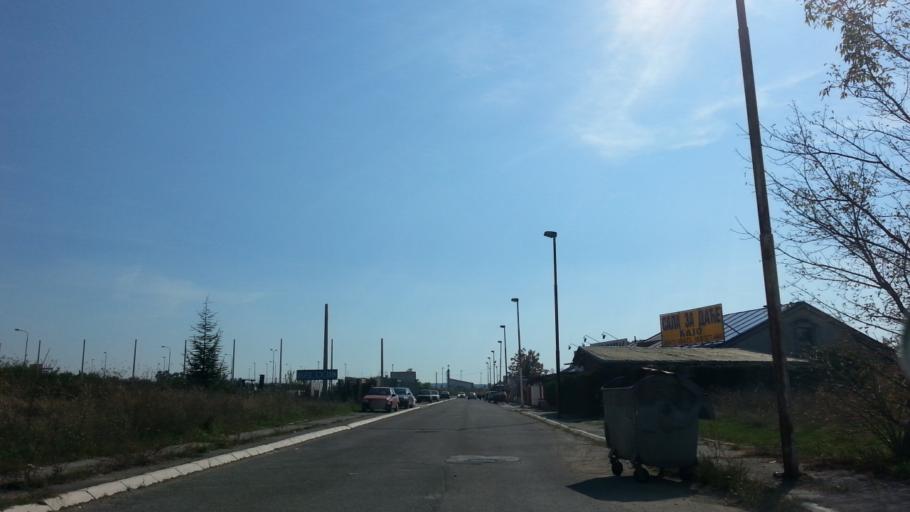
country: RS
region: Central Serbia
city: Sremcica
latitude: 44.7087
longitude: 20.4124
